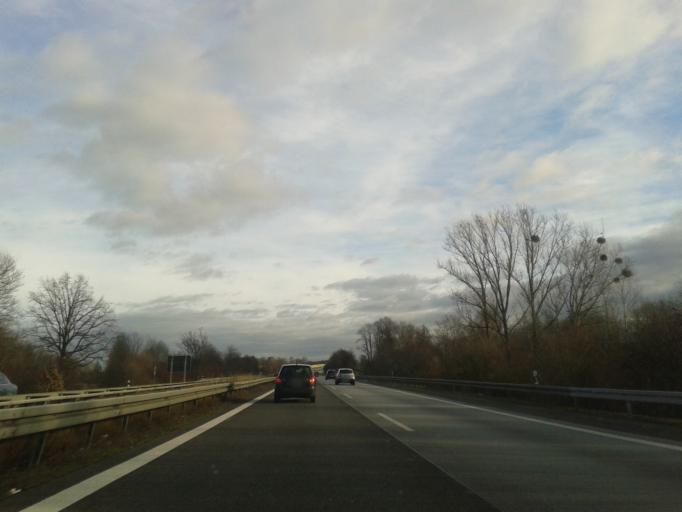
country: DE
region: Saxony
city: Goda
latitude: 51.2025
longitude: 14.2957
